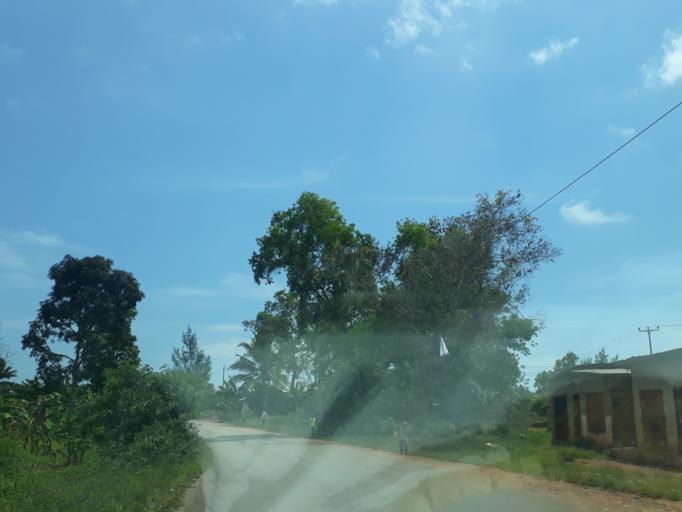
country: TZ
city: Kiwengwa
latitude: -5.9949
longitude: 39.3460
